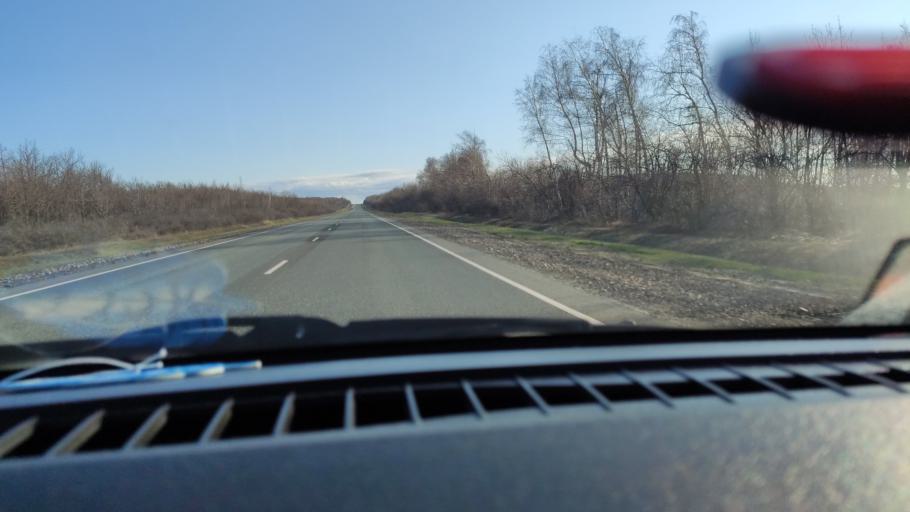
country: RU
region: Saratov
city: Khvalynsk
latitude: 52.6125
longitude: 48.1611
